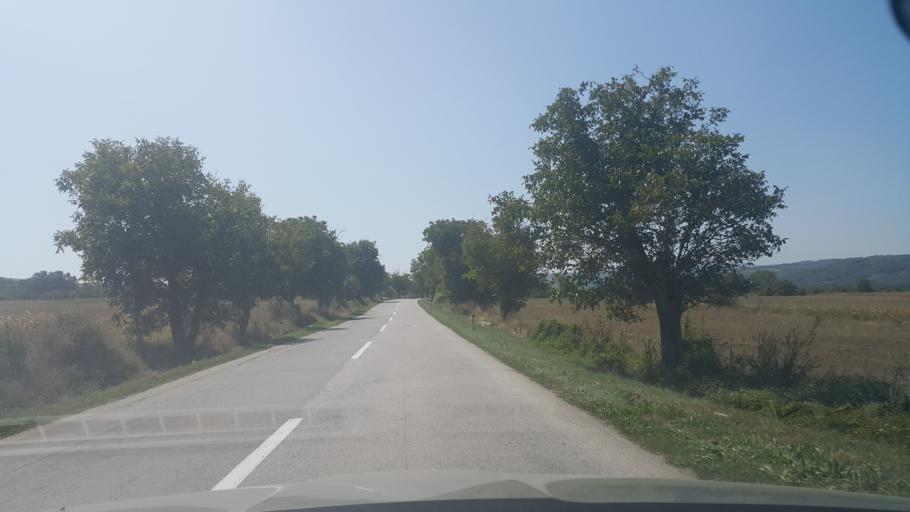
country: RS
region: Central Serbia
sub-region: Zajecarski Okrug
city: Knjazevac
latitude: 43.7022
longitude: 22.3013
